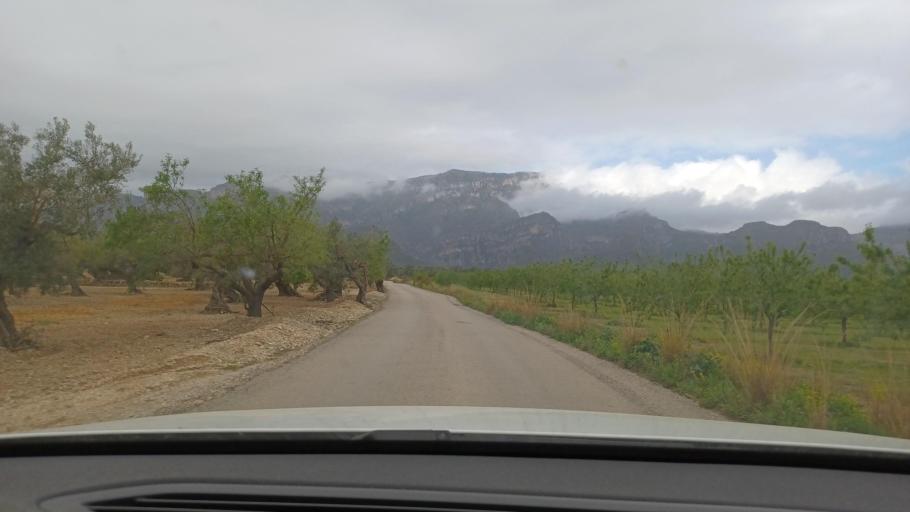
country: ES
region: Catalonia
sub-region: Provincia de Tarragona
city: Mas de Barberans
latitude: 40.7973
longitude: 0.4297
